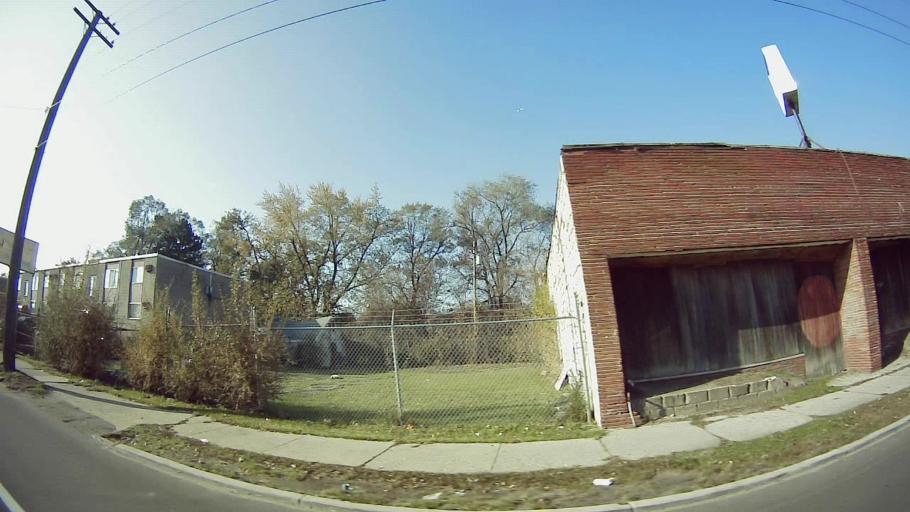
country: US
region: Michigan
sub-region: Oakland County
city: Oak Park
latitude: 42.3991
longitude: -83.1790
